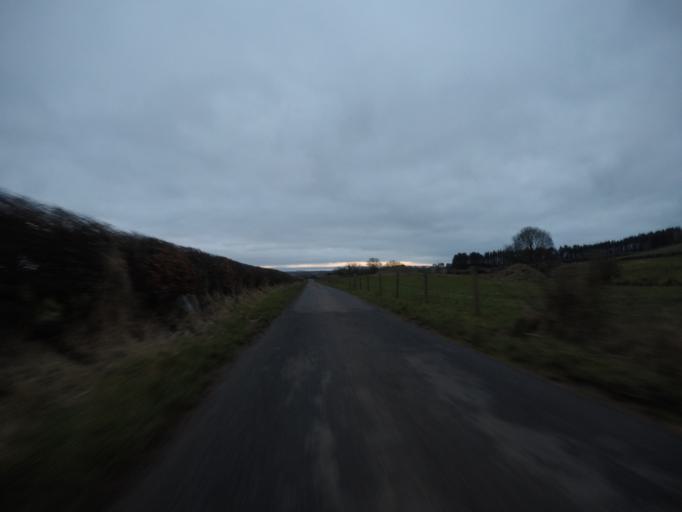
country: GB
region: Scotland
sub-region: North Ayrshire
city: Dalry
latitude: 55.6796
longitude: -4.7257
